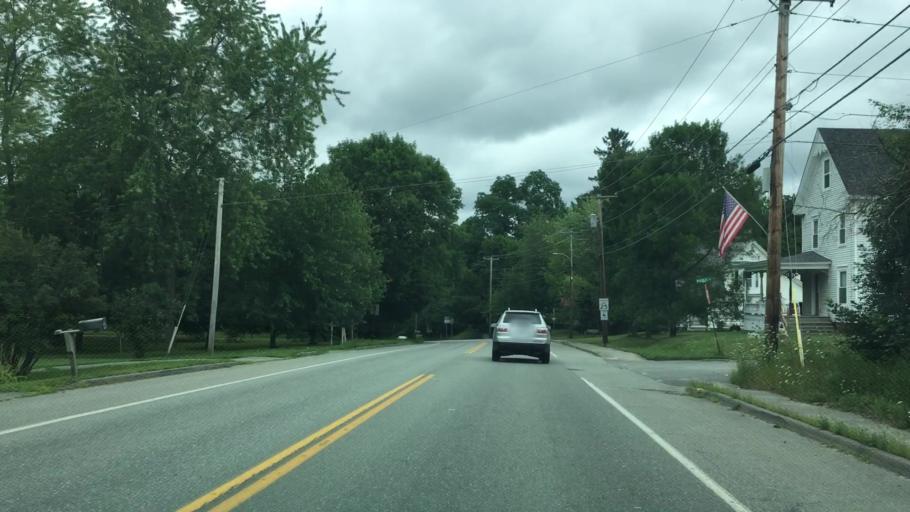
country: US
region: Maine
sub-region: Penobscot County
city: Bangor
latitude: 44.7644
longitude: -68.7840
